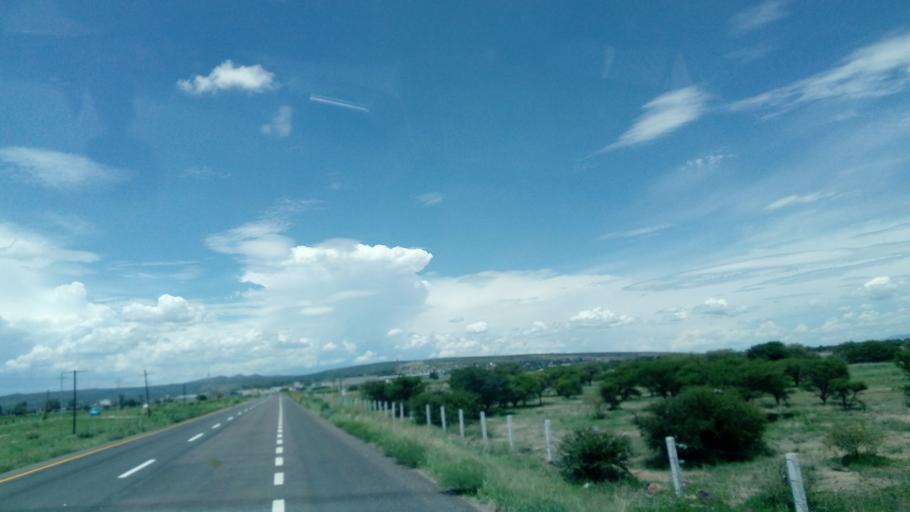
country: MX
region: Durango
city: Victoria de Durango
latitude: 24.0867
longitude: -104.5632
